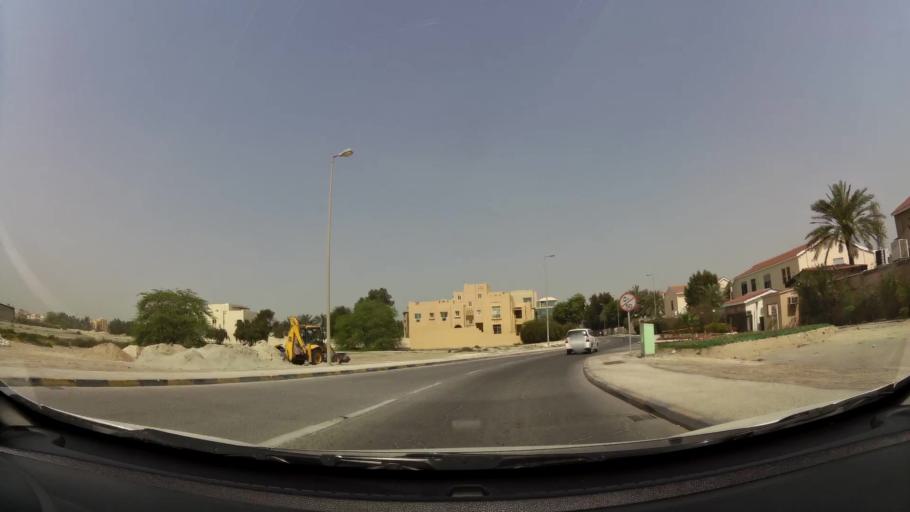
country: BH
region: Manama
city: Jidd Hafs
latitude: 26.2176
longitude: 50.4787
